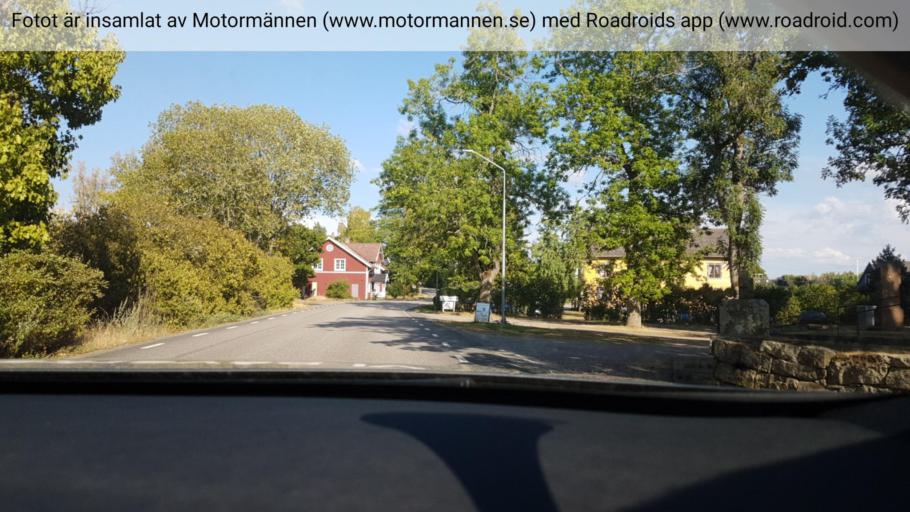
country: SE
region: Vaestra Goetaland
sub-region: Gotene Kommun
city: Goetene
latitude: 58.6202
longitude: 13.4904
